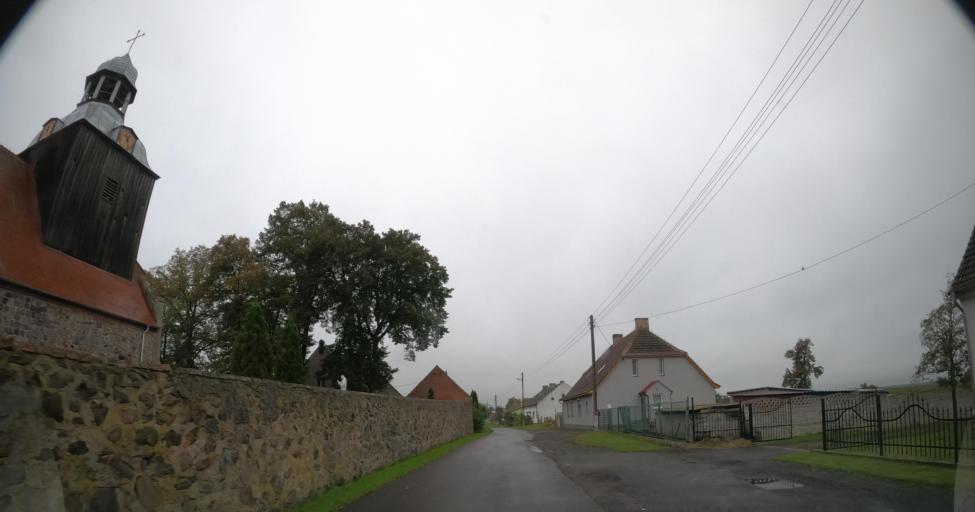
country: PL
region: West Pomeranian Voivodeship
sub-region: Powiat pyrzycki
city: Kozielice
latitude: 53.0466
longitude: 14.7724
